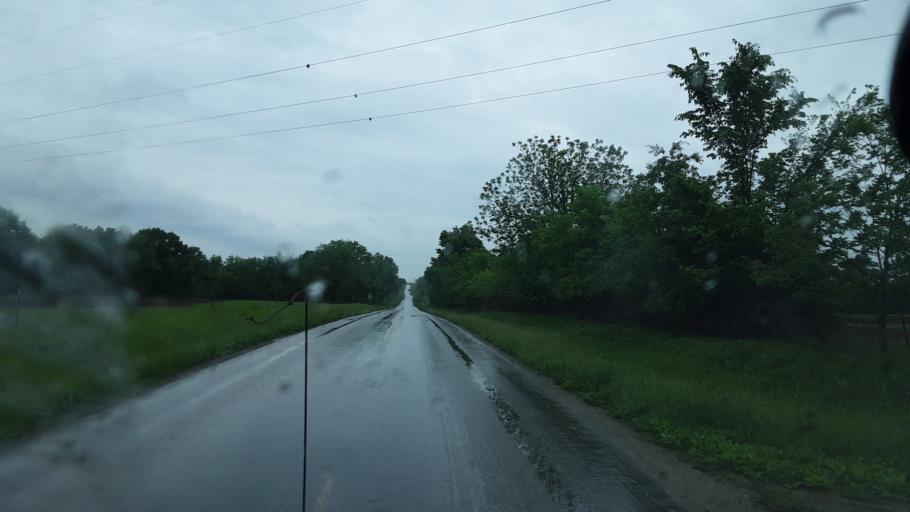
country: US
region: Missouri
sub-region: Randolph County
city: Moberly
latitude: 39.3602
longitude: -92.2682
